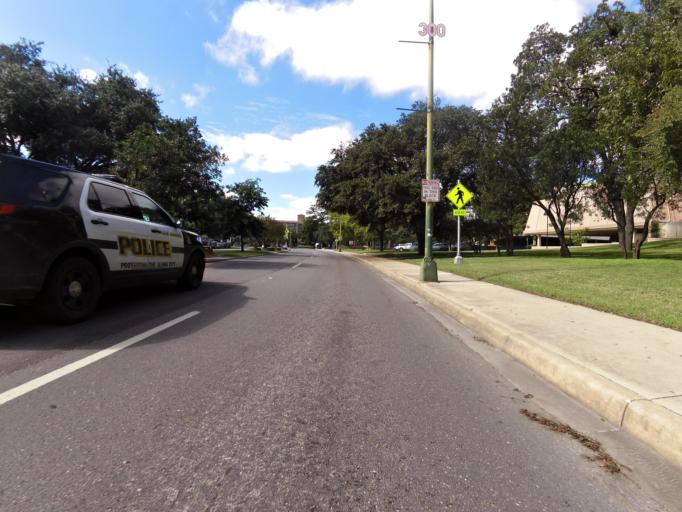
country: US
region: Texas
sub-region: Bexar County
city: San Antonio
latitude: 29.4181
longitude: -98.4862
